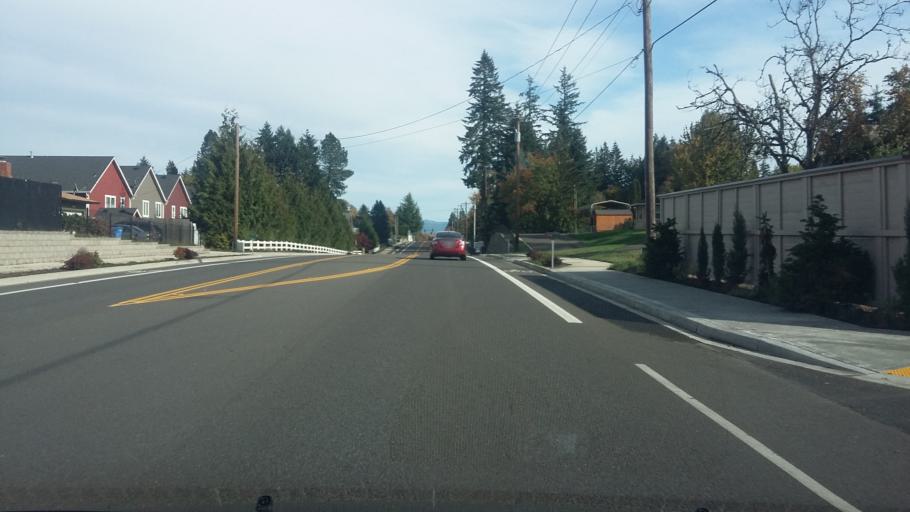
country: US
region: Washington
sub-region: Clark County
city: Salmon Creek
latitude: 45.6859
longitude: -122.6307
